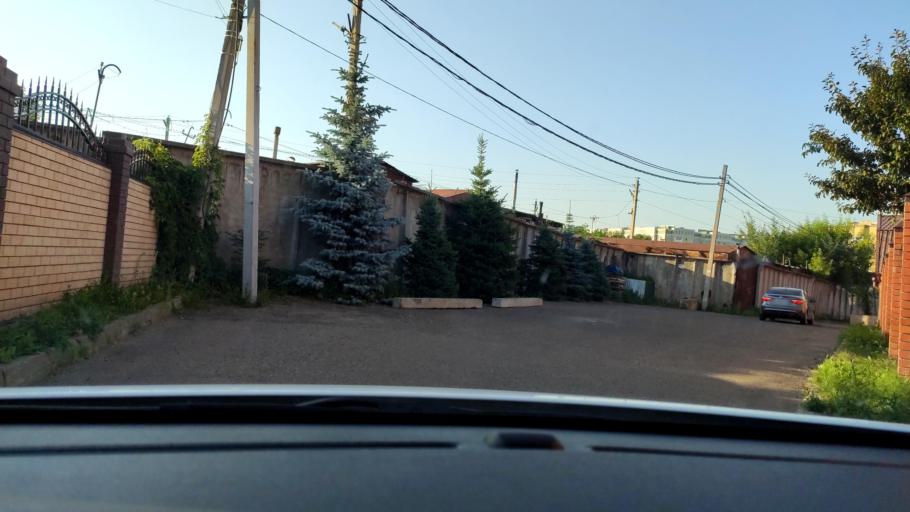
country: RU
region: Tatarstan
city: Stolbishchi
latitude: 55.7478
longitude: 49.2427
